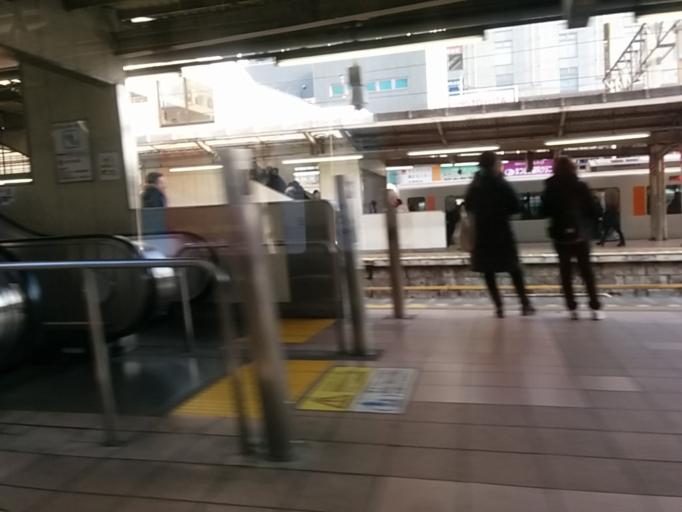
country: JP
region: Saitama
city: Asaka
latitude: 35.8143
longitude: 139.5872
